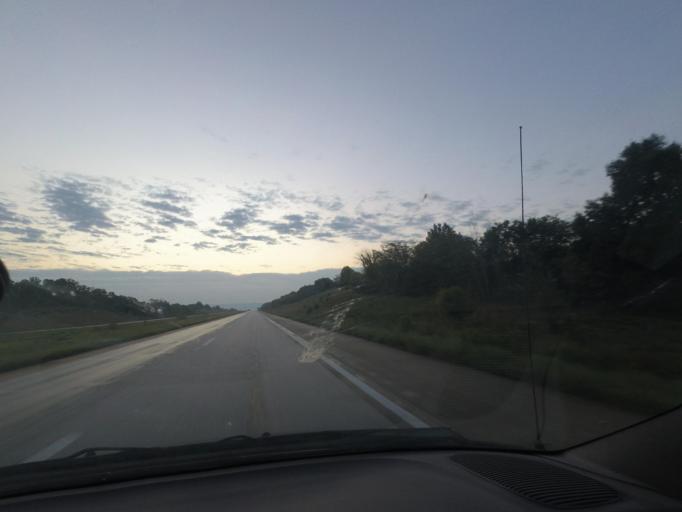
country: US
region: Missouri
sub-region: Macon County
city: Macon
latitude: 39.7589
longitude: -92.6581
